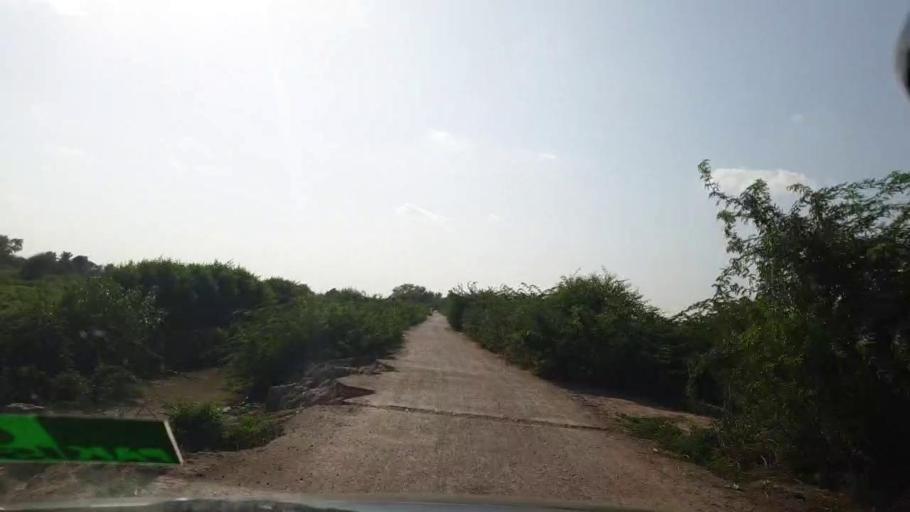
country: PK
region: Sindh
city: Tando Bago
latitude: 24.7118
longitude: 69.1961
